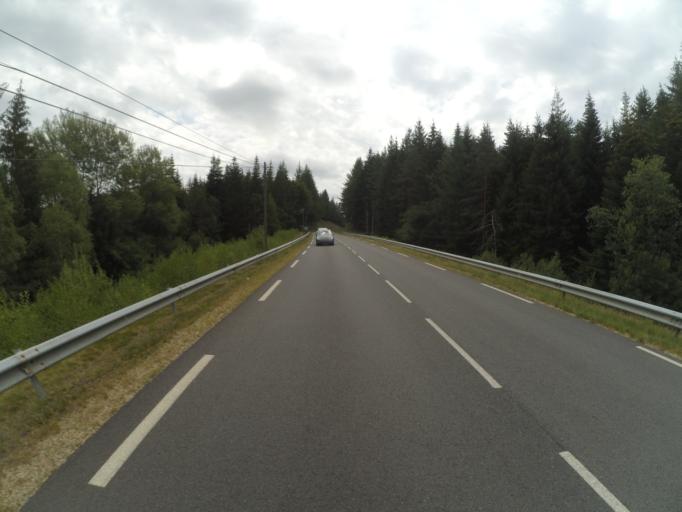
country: FR
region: Limousin
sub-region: Departement de la Creuse
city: La Courtine
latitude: 45.6481
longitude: 2.2684
